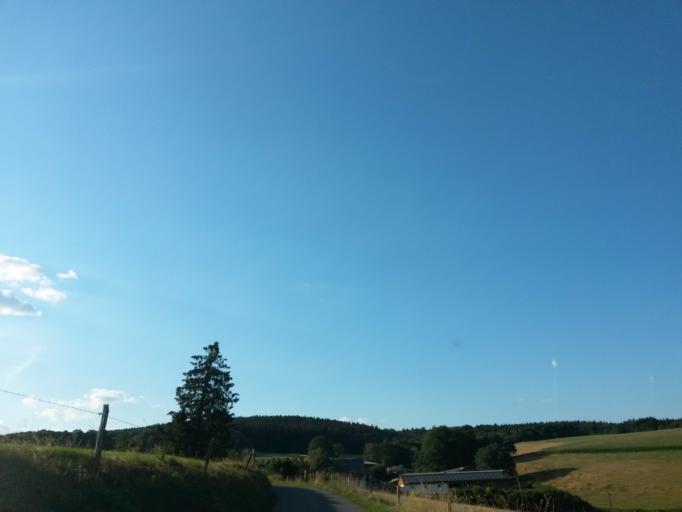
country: DE
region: North Rhine-Westphalia
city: Meinerzhagen
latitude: 51.1068
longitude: 7.6953
